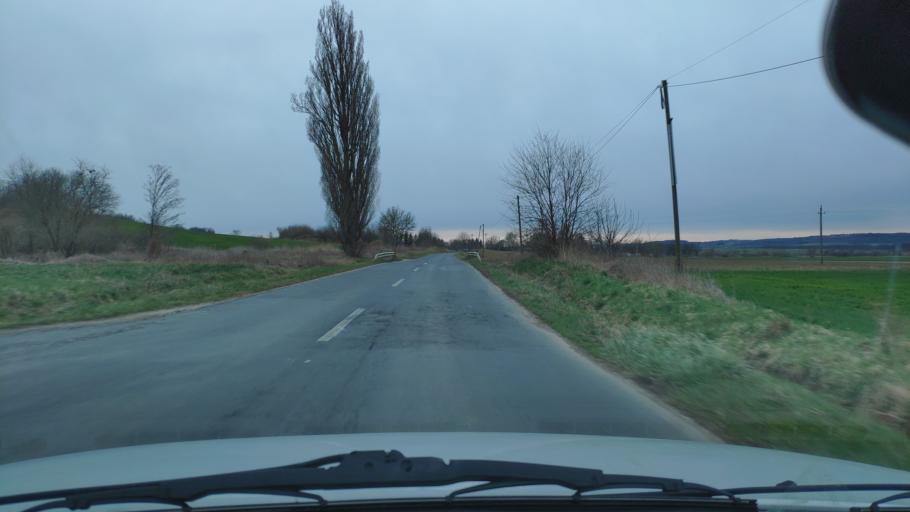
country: HU
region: Zala
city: Nagykanizsa
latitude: 46.5516
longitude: 16.9889
